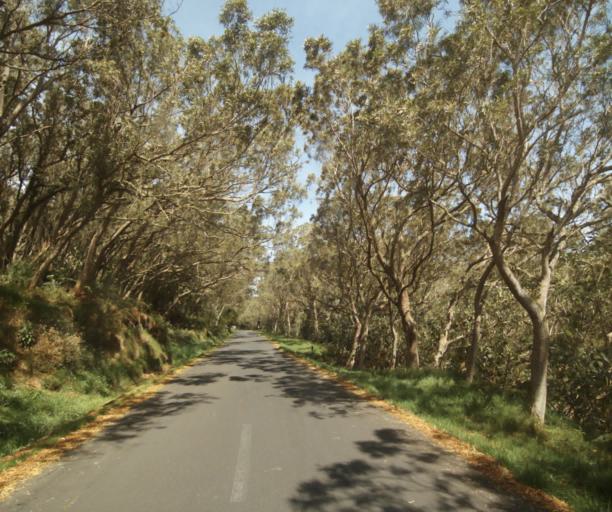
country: RE
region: Reunion
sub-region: Reunion
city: Trois-Bassins
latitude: -21.0587
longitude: 55.3644
